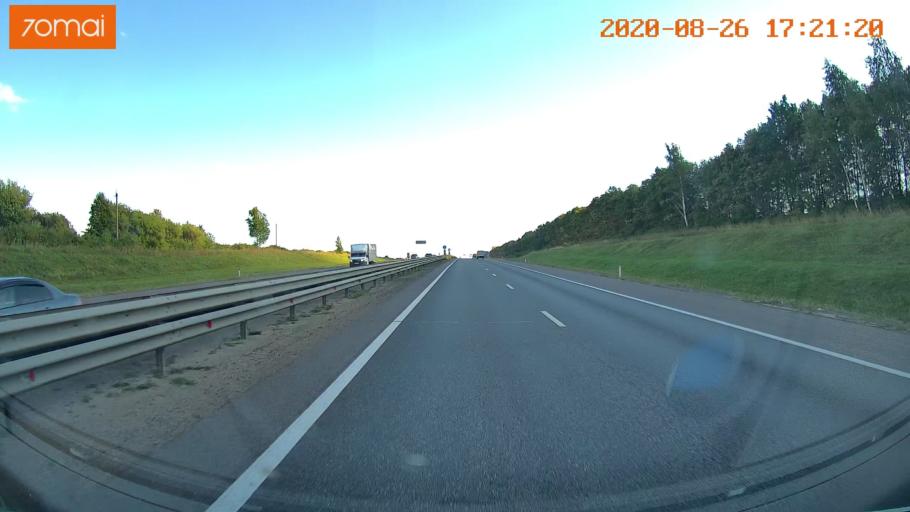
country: RU
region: Tula
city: Volovo
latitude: 53.5666
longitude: 38.1120
